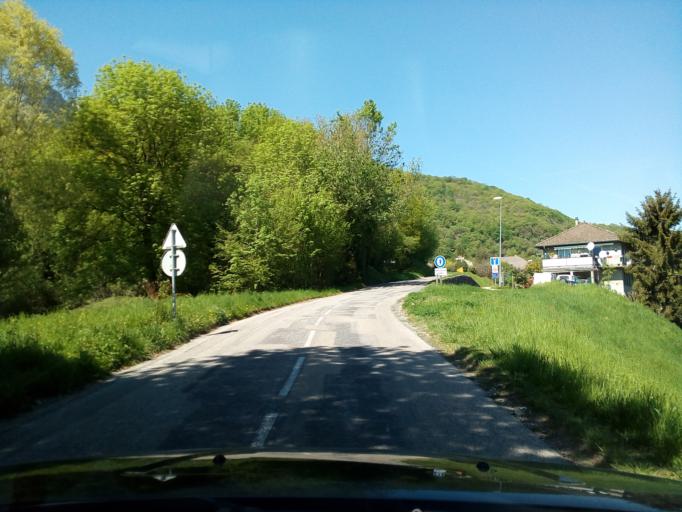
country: FR
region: Rhone-Alpes
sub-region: Departement de l'Isere
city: Chapareillan
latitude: 45.4659
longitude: 5.9856
